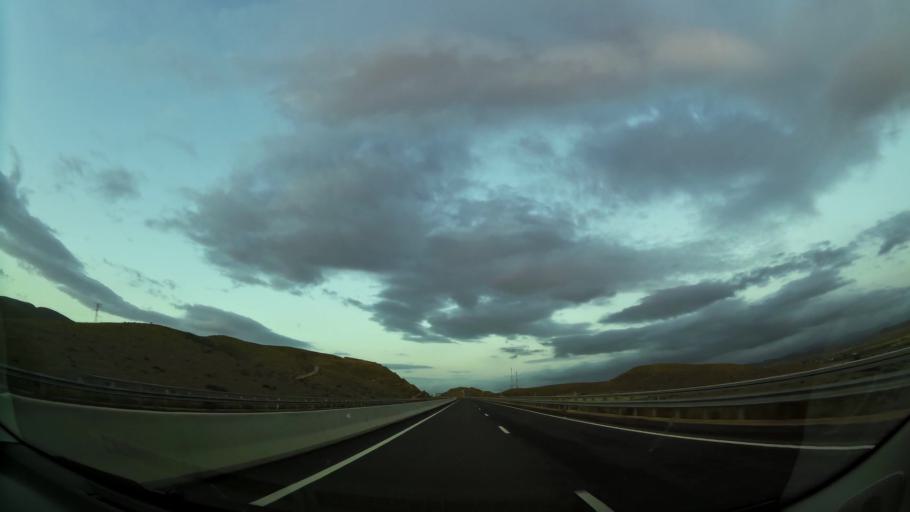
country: MA
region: Oriental
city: El Aioun
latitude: 34.5947
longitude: -2.6713
